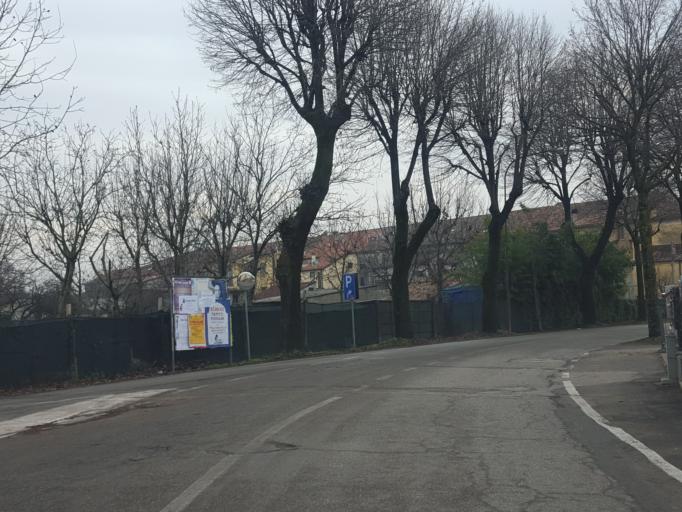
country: IT
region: Veneto
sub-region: Provincia di Verona
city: Arcole
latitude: 45.3601
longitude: 11.2847
